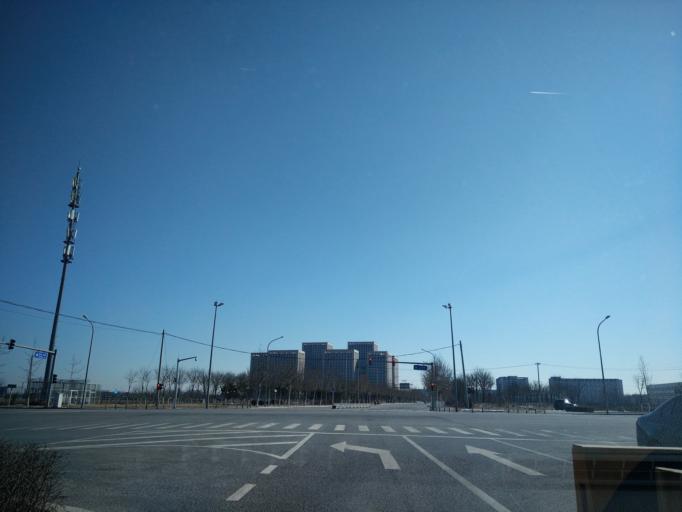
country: CN
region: Beijing
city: Yinghai
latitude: 39.7510
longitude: 116.4888
